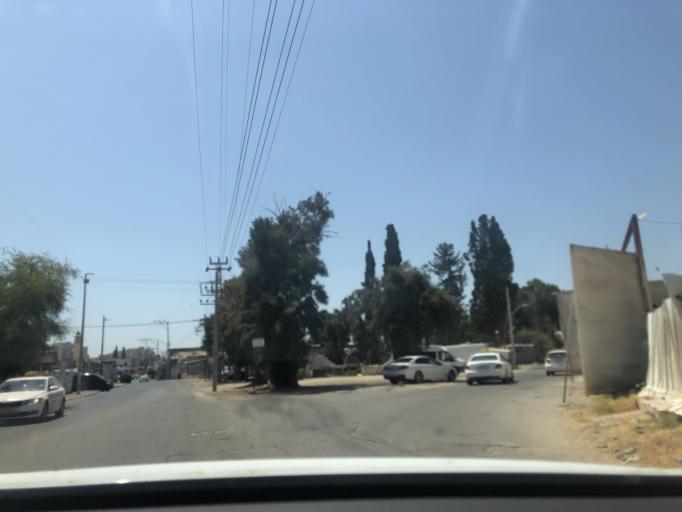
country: IL
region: Central District
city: Lod
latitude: 31.9569
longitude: 34.8996
